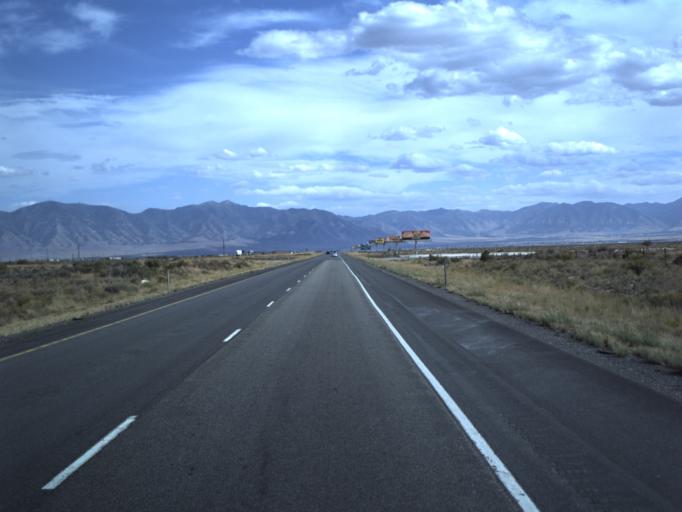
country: US
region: Utah
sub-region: Tooele County
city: Grantsville
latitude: 40.6941
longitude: -112.4718
